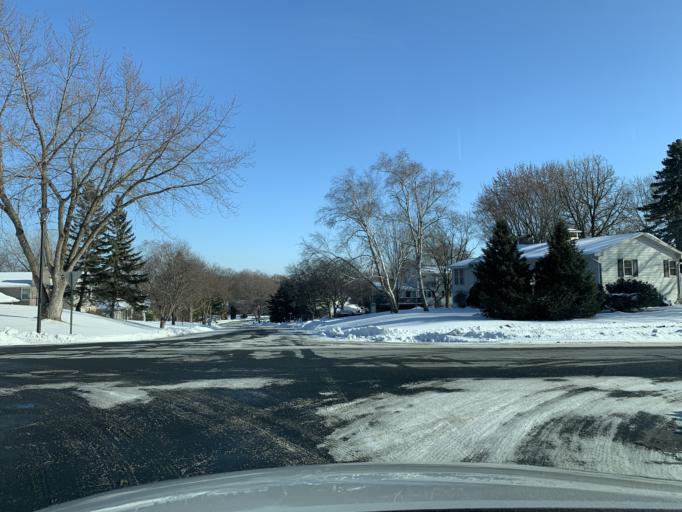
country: US
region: Minnesota
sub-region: Hennepin County
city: Bloomington
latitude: 44.8241
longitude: -93.3384
